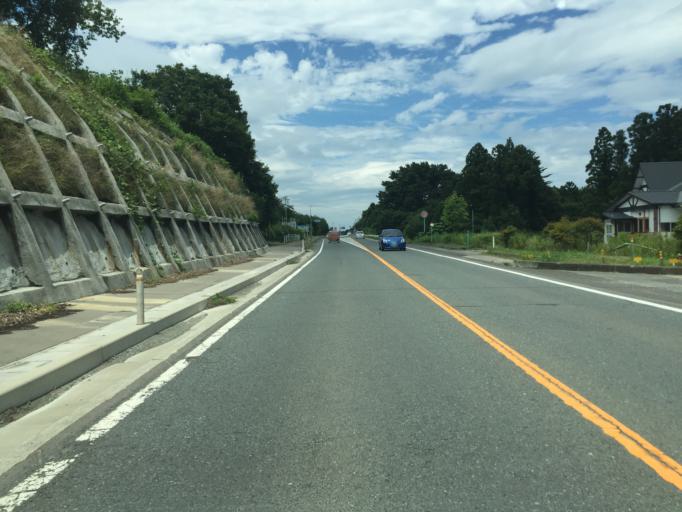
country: JP
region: Miyagi
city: Marumori
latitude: 37.7409
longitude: 140.9540
